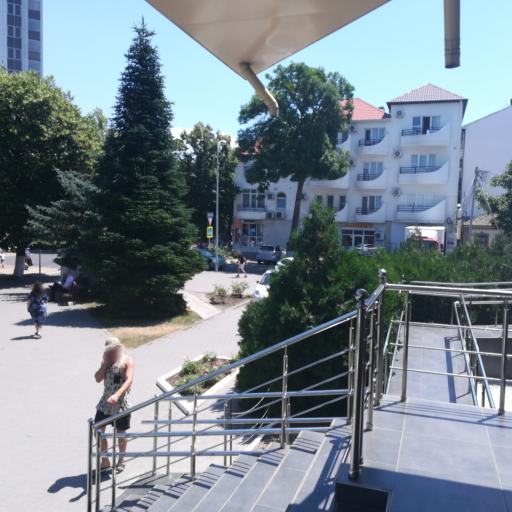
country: RU
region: Krasnodarskiy
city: Anapa
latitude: 44.8943
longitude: 37.3077
